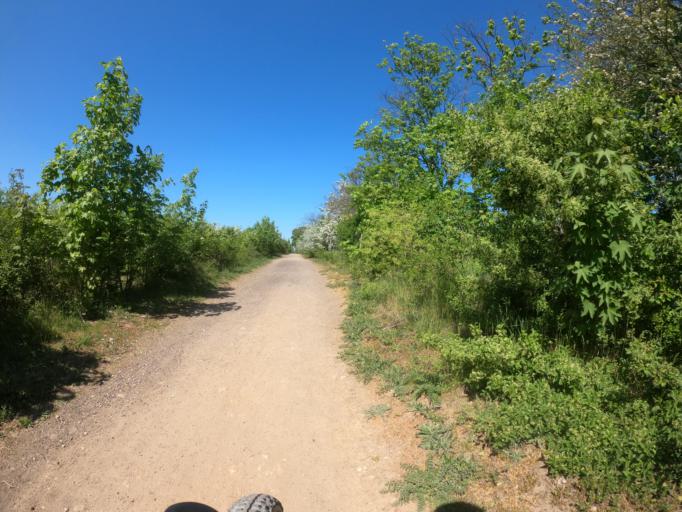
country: DE
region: Hesse
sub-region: Regierungsbezirk Darmstadt
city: Florsheim
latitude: 50.0091
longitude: 8.3971
